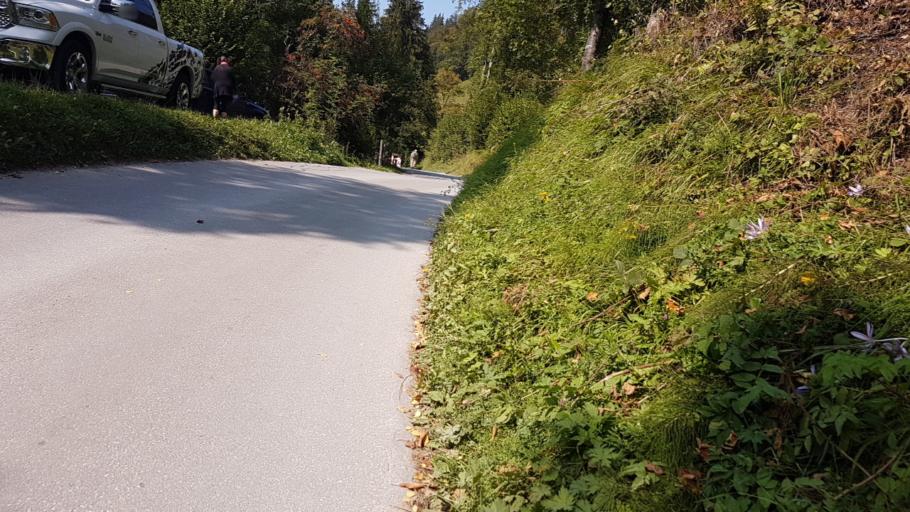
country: CH
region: Bern
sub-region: Frutigen-Niedersimmental District
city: Aeschi
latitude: 46.6345
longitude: 7.7383
